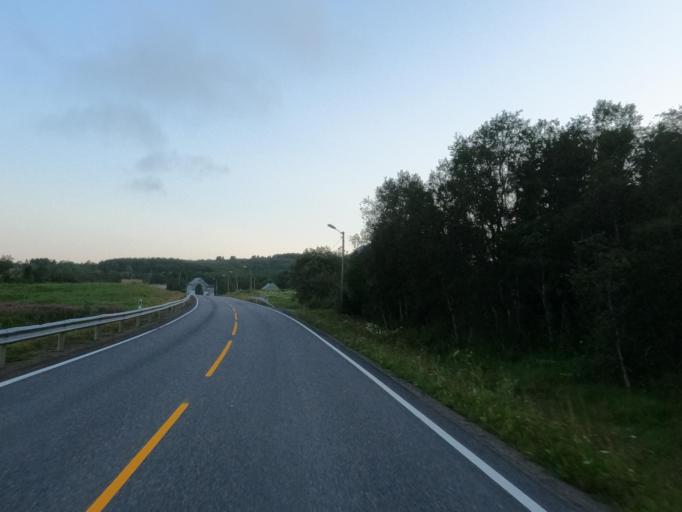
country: NO
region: Nordland
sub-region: Tjeldsund
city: Hol
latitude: 68.5656
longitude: 16.3128
